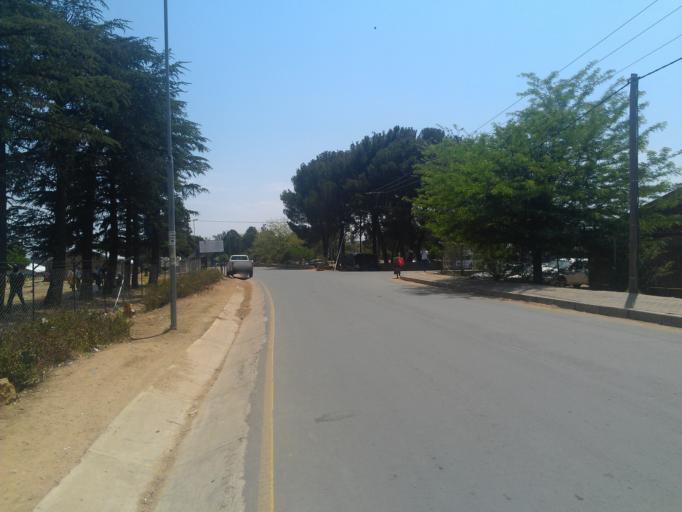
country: LS
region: Berea
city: Teyateyaneng
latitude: -29.1461
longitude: 27.7405
